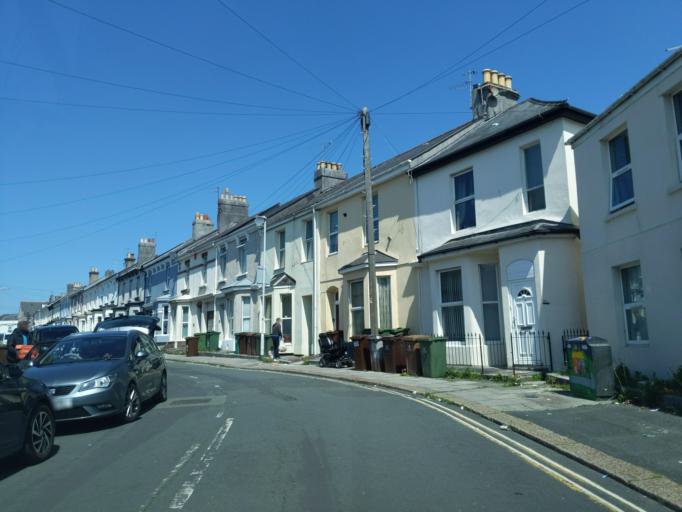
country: GB
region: England
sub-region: Plymouth
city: Plymouth
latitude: 50.3747
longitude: -4.1463
